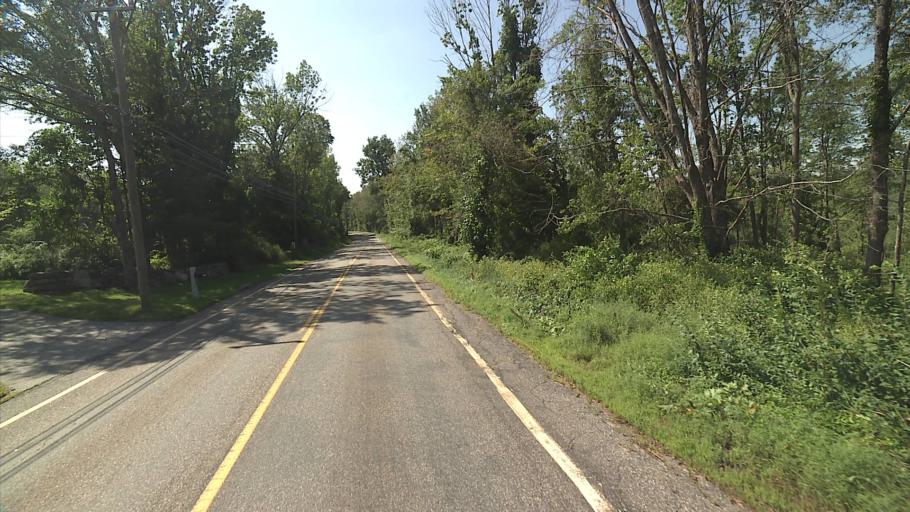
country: US
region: Connecticut
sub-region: Tolland County
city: Storrs
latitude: 41.9111
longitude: -72.1733
